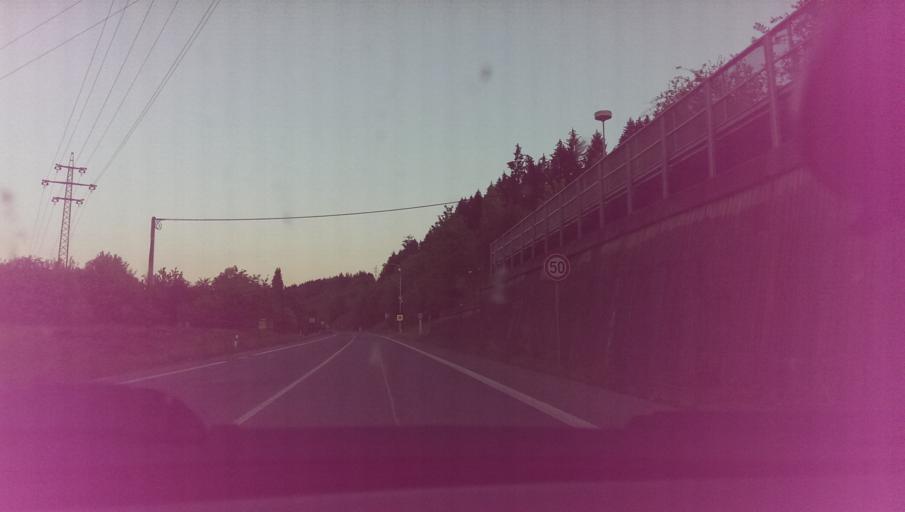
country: CZ
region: Zlin
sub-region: Okres Vsetin
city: Vsetin
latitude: 49.3419
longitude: 17.9738
